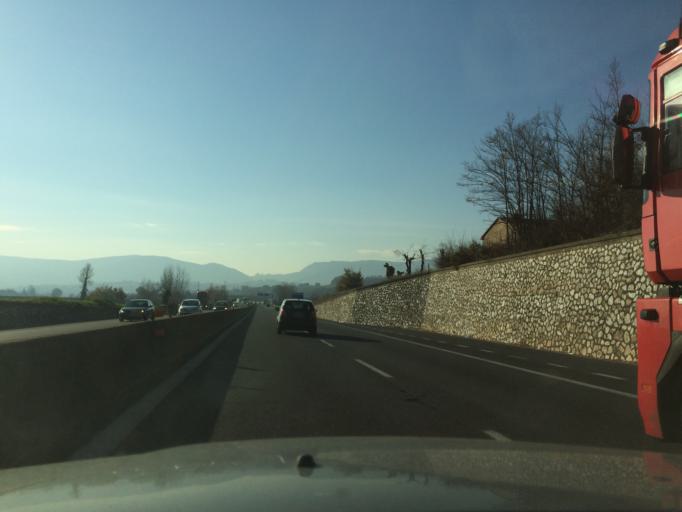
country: IT
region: Umbria
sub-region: Provincia di Terni
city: Narni Scalo
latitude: 42.5612
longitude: 12.5448
